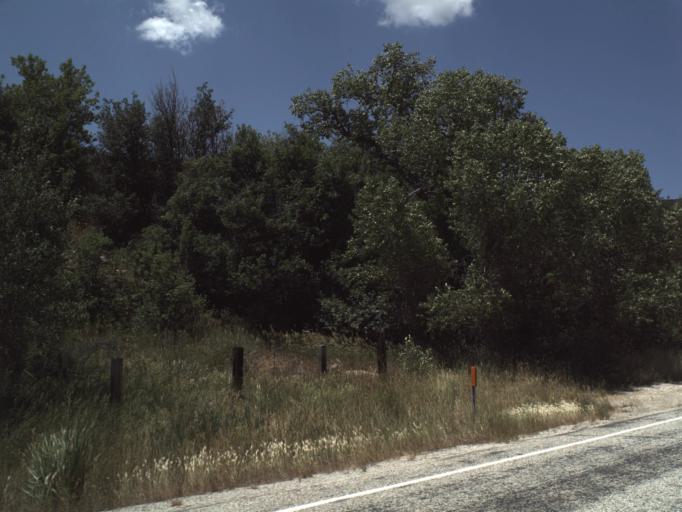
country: US
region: Utah
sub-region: Weber County
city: Wolf Creek
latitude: 41.3194
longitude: -111.6157
